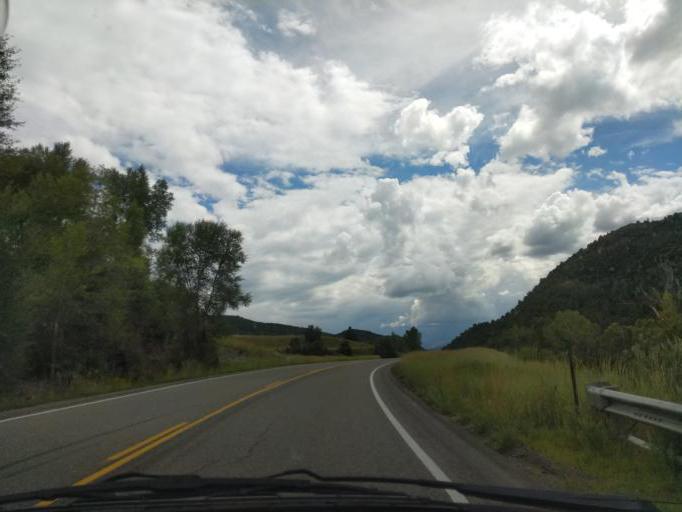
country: US
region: Colorado
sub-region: Delta County
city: Paonia
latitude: 39.0525
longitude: -107.3612
